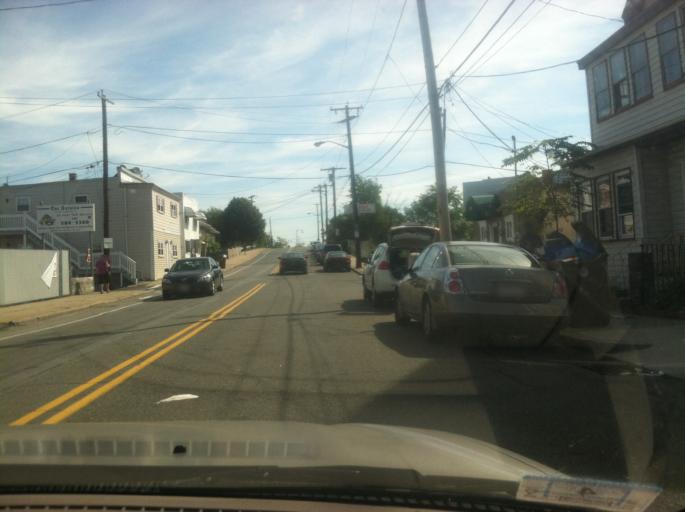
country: US
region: Massachusetts
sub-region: Suffolk County
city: Revere
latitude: 42.4188
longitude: -70.9903
